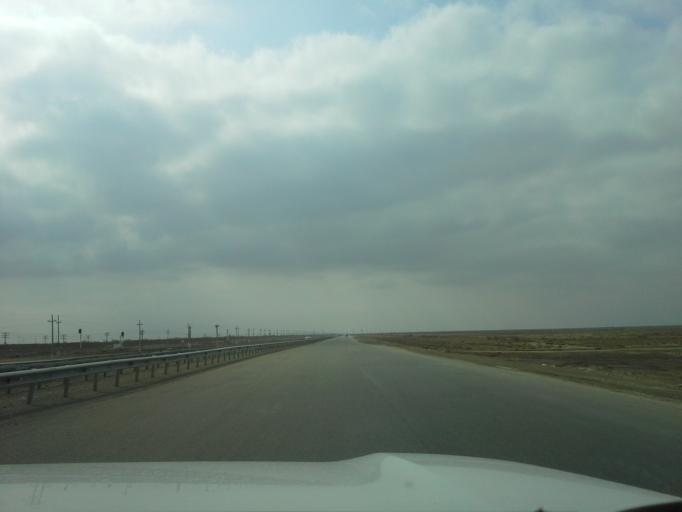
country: TM
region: Ahal
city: Tejen
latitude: 37.2247
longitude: 60.1336
